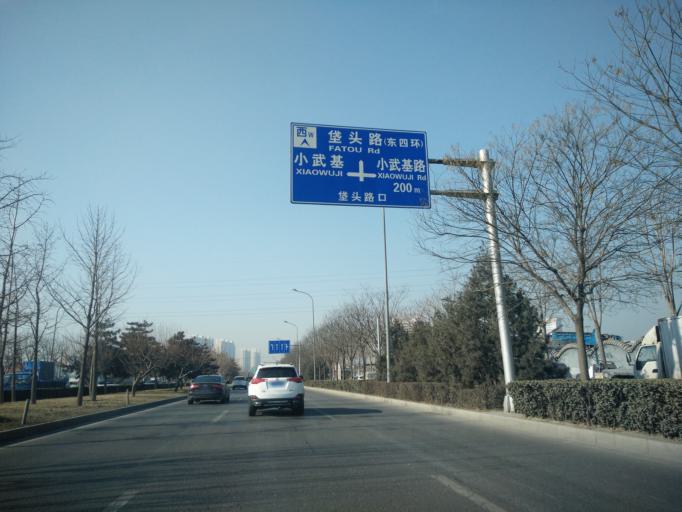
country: CN
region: Beijing
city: Longtan
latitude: 39.8598
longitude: 116.4882
